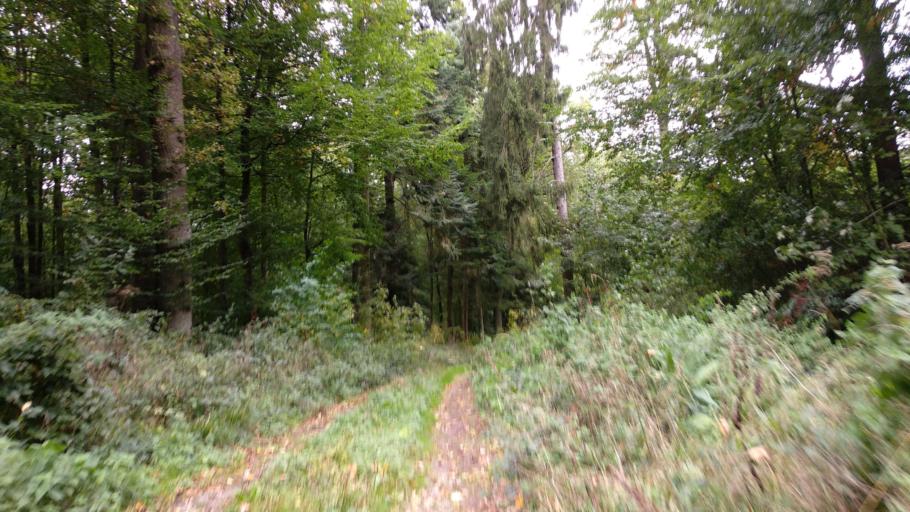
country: DE
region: North Rhine-Westphalia
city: Beverungen
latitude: 51.6907
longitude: 9.3721
